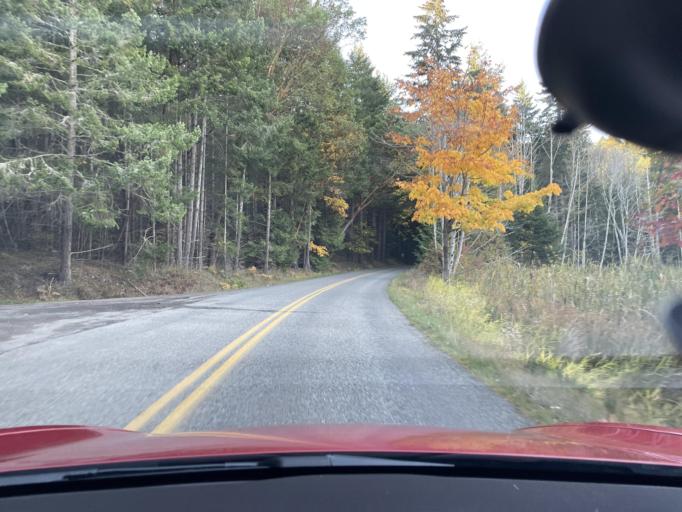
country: US
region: Washington
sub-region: San Juan County
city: Friday Harbor
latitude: 48.5228
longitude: -123.1454
